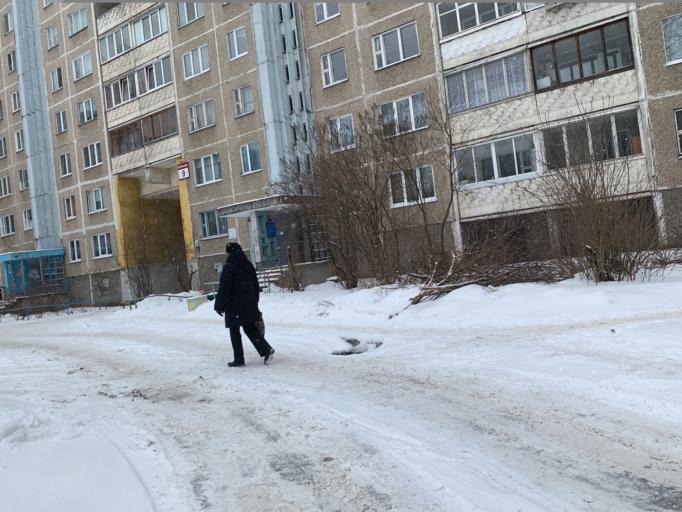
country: BY
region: Minsk
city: Borovlyany
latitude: 53.9544
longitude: 27.6315
